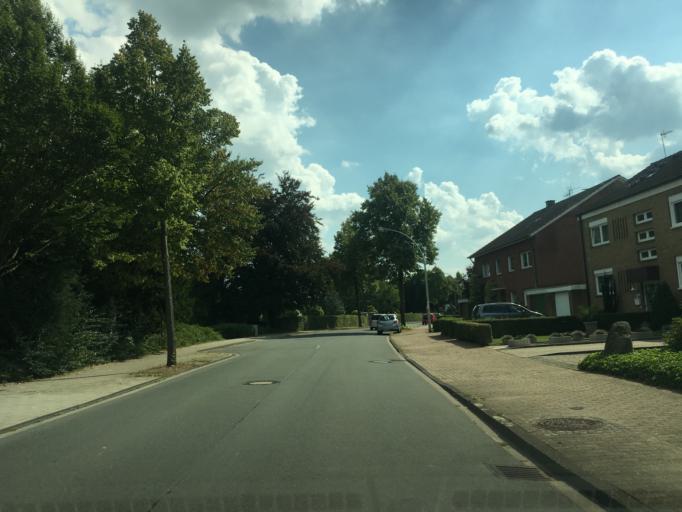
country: DE
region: North Rhine-Westphalia
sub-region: Regierungsbezirk Munster
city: Muenster
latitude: 51.8816
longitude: 7.6080
